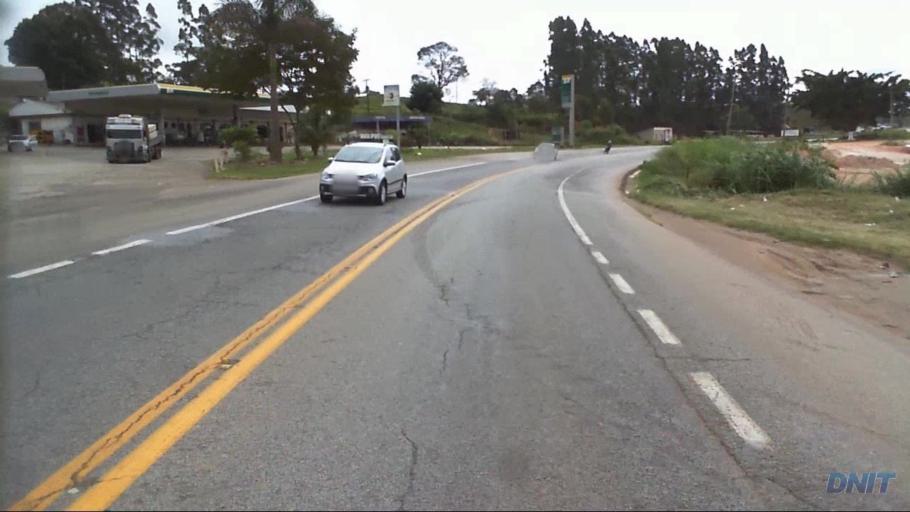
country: BR
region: Minas Gerais
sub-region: Caete
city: Caete
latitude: -19.7415
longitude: -43.5550
